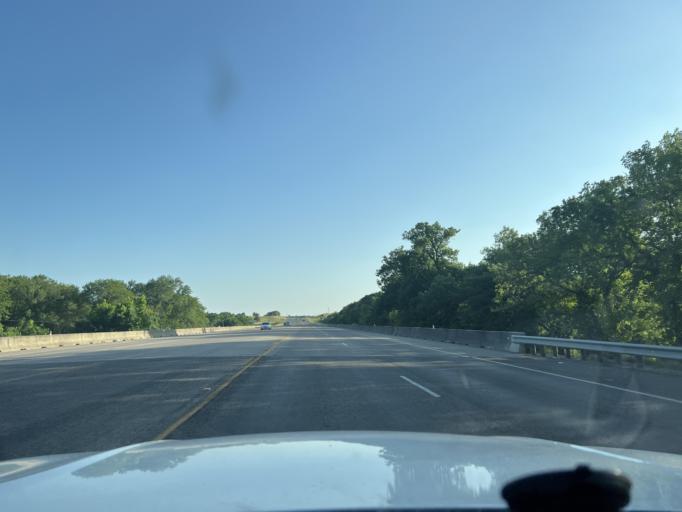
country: US
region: Texas
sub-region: Washington County
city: Brenham
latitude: 30.1966
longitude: -96.3649
